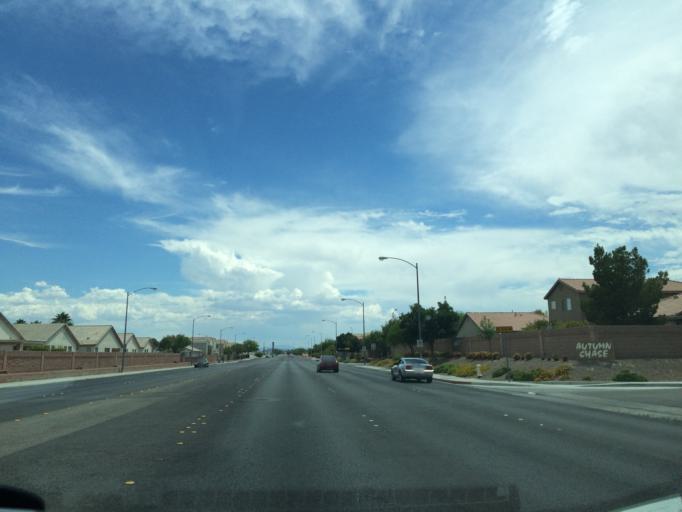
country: US
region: Nevada
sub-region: Clark County
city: North Las Vegas
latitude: 36.2523
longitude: -115.1801
